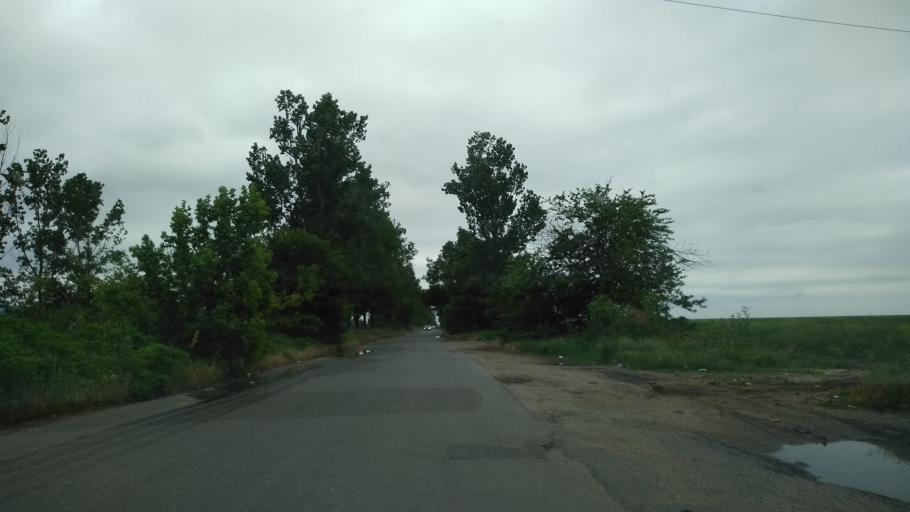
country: RO
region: Giurgiu
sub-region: Comuna Herasti
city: Herasti
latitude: 44.2501
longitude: 26.3678
